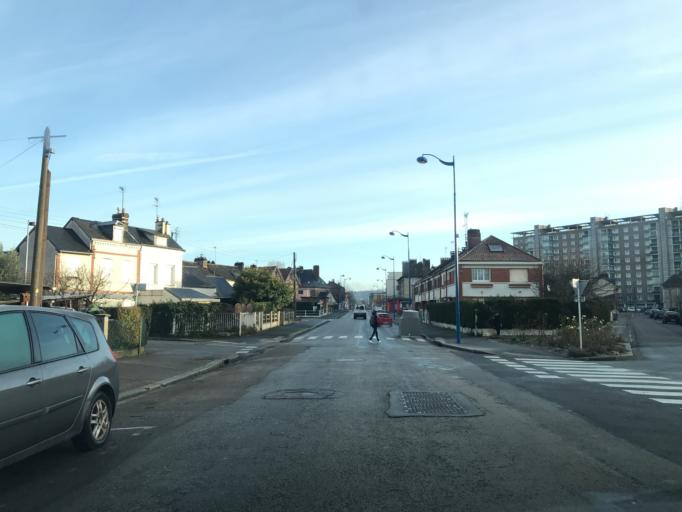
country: FR
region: Haute-Normandie
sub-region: Departement de la Seine-Maritime
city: Sotteville-les-Rouen
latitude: 49.4176
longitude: 1.0886
